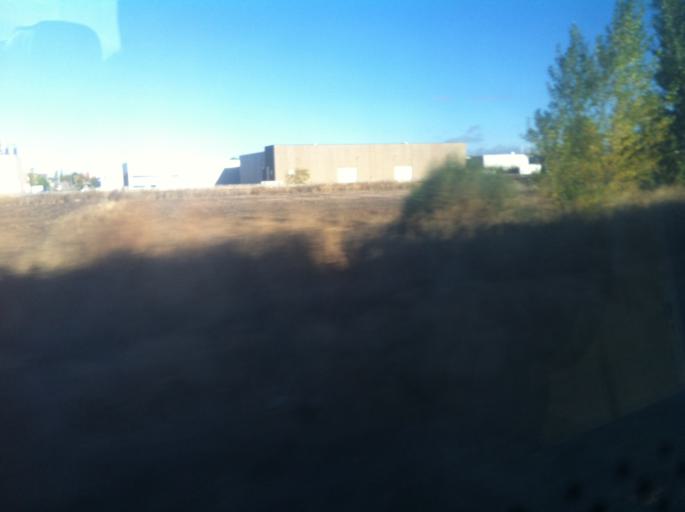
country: ES
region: Castille and Leon
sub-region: Provincia de Palencia
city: Venta de Banos
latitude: 41.9312
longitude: -4.4800
